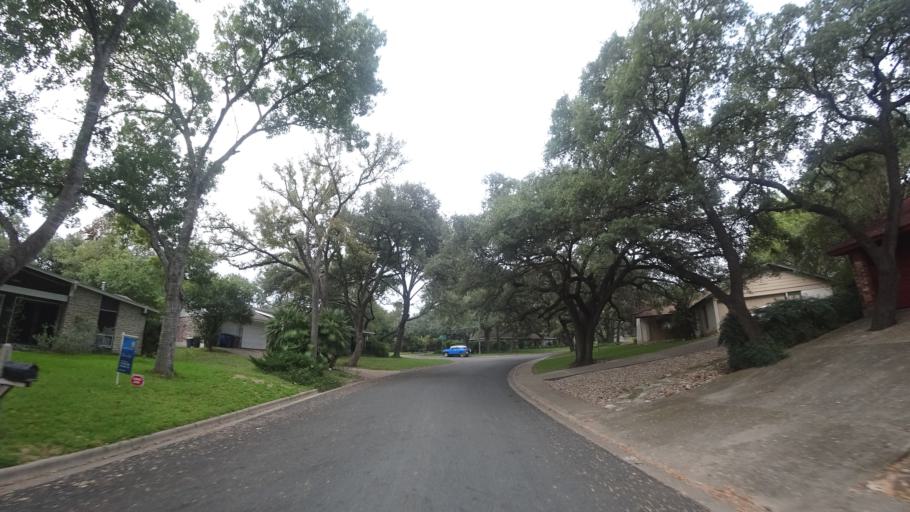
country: US
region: Texas
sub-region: Travis County
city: Austin
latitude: 30.3467
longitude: -97.6914
